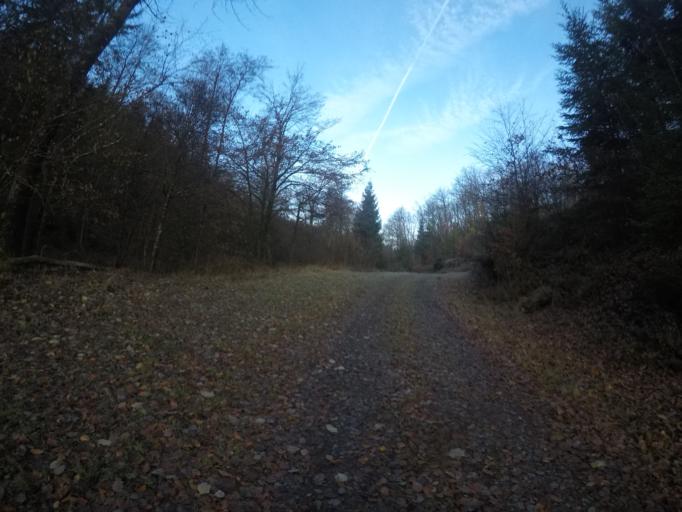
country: BE
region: Wallonia
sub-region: Province du Luxembourg
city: Habay-la-Vieille
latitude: 49.7436
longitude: 5.6720
